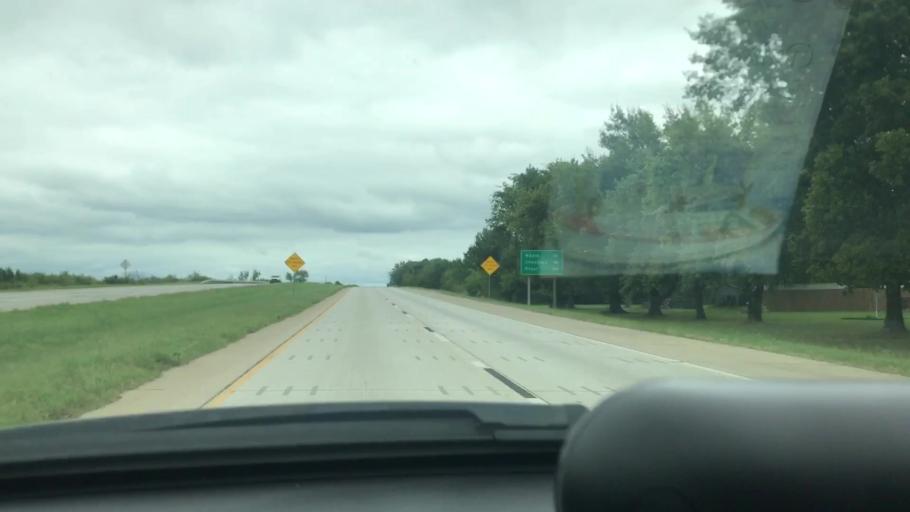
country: US
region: Oklahoma
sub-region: Wagoner County
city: Wagoner
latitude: 35.9668
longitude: -95.3904
